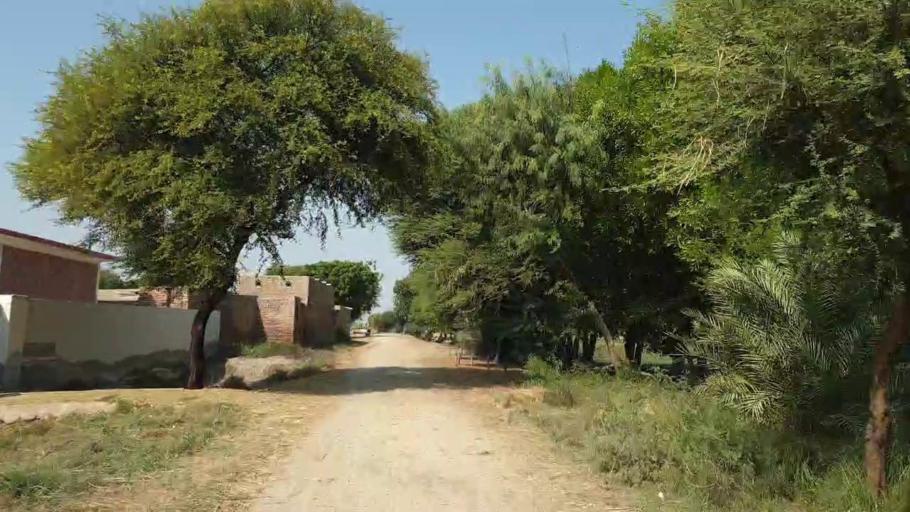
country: PK
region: Sindh
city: Tando Muhammad Khan
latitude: 25.0283
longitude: 68.4076
